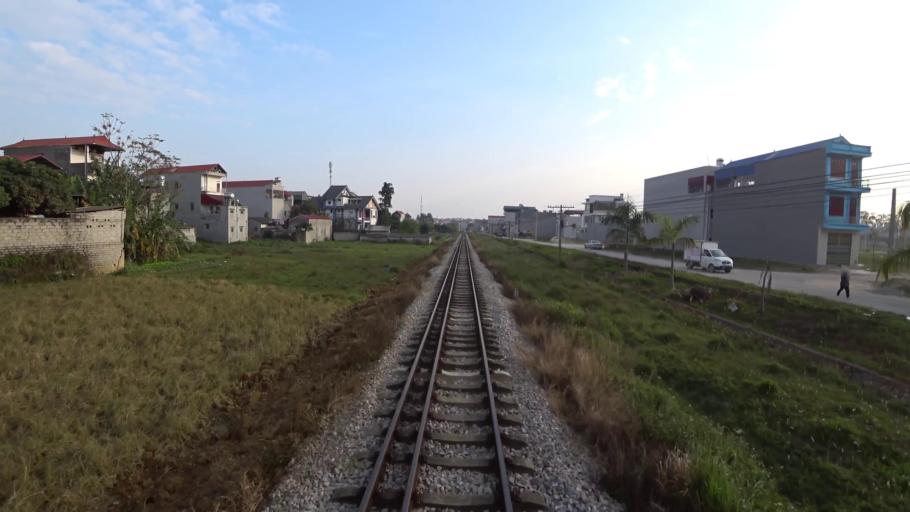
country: VN
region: Lang Son
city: Thi Tran Cao Loc
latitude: 21.8812
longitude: 106.7492
